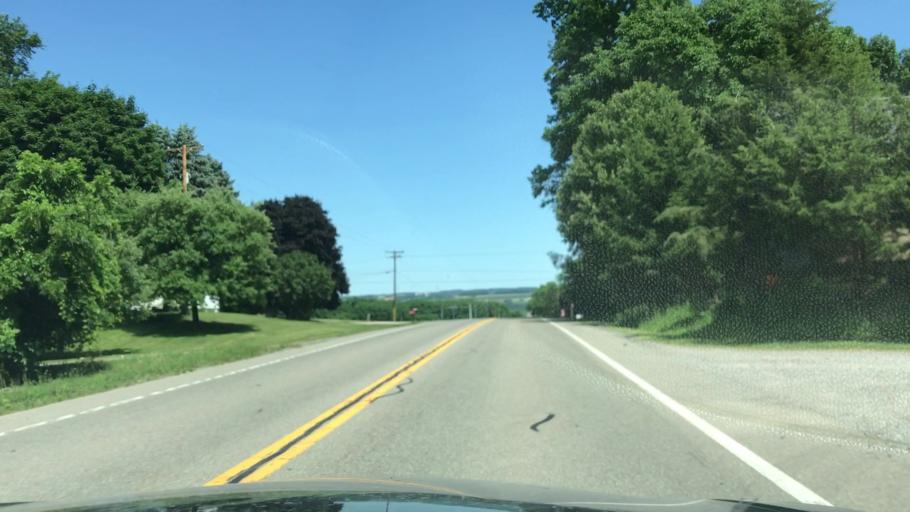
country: US
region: New York
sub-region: Livingston County
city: Mount Morris
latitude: 42.7563
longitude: -77.8935
